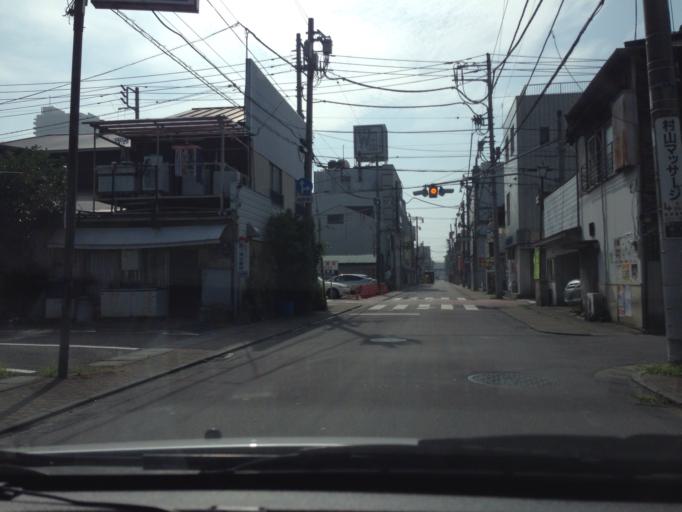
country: JP
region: Ibaraki
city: Naka
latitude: 36.0780
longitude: 140.1990
